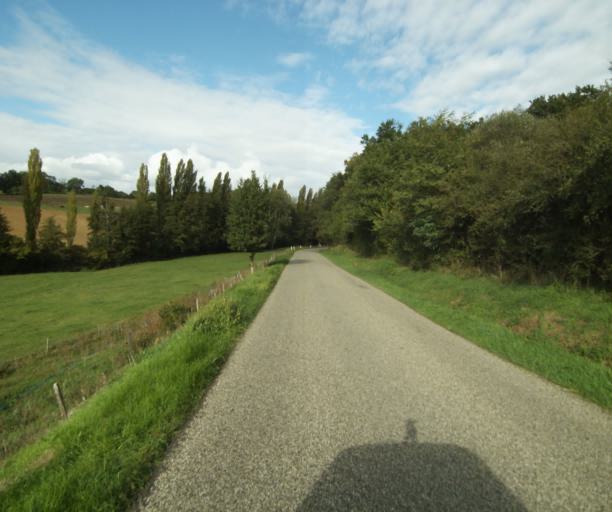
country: FR
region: Midi-Pyrenees
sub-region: Departement du Gers
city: Eauze
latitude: 43.8938
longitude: 0.0941
